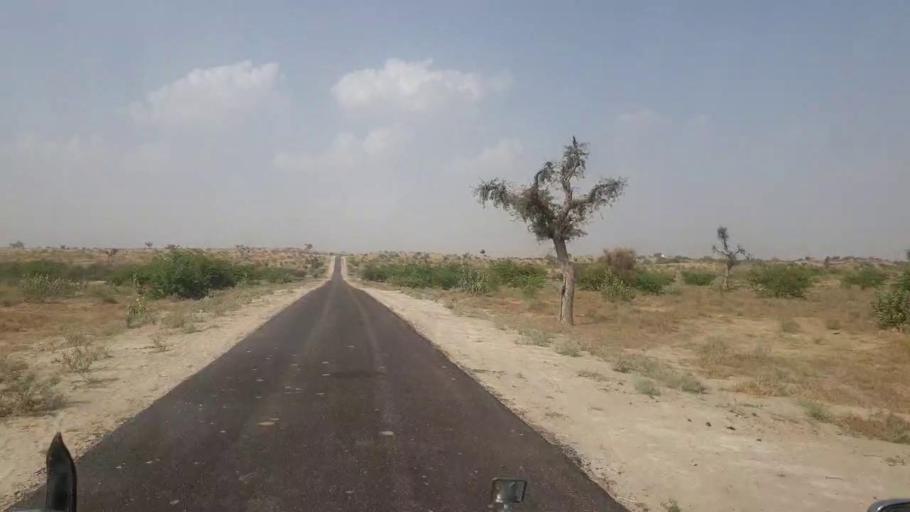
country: PK
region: Sindh
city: Islamkot
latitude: 25.2063
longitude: 70.2834
